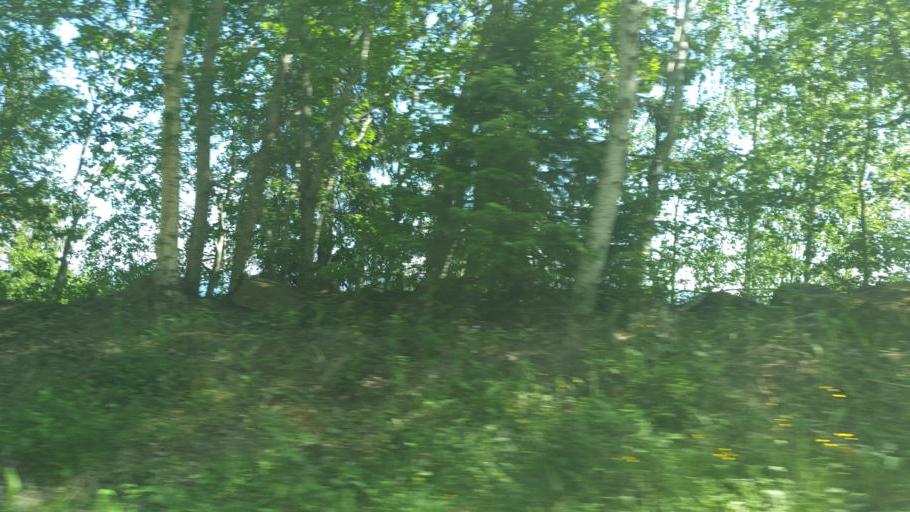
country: NO
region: Nord-Trondelag
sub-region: Frosta
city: Frosta
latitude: 63.7060
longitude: 10.7577
